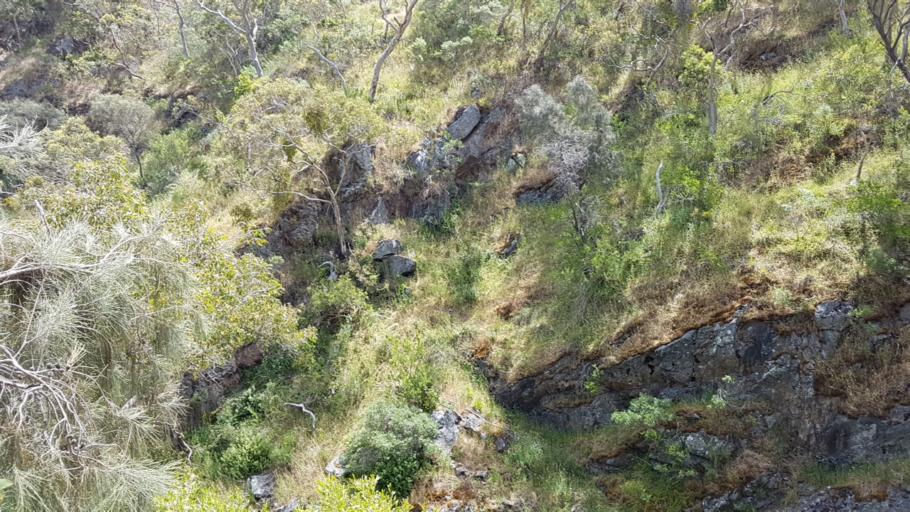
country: AU
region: South Australia
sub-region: Alexandrina
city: Mount Compass
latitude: -35.4434
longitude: 138.5839
